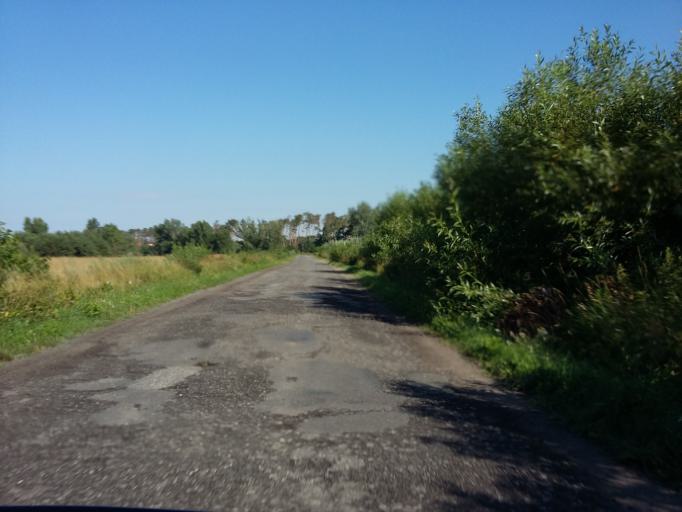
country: AT
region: Lower Austria
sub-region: Politischer Bezirk Ganserndorf
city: Drosing
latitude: 48.4945
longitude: 16.9633
